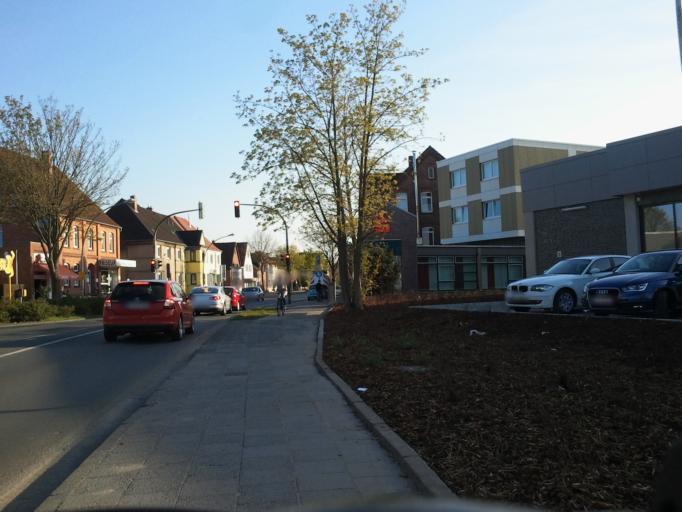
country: DE
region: Lower Saxony
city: Nienburg
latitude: 52.6520
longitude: 9.2173
